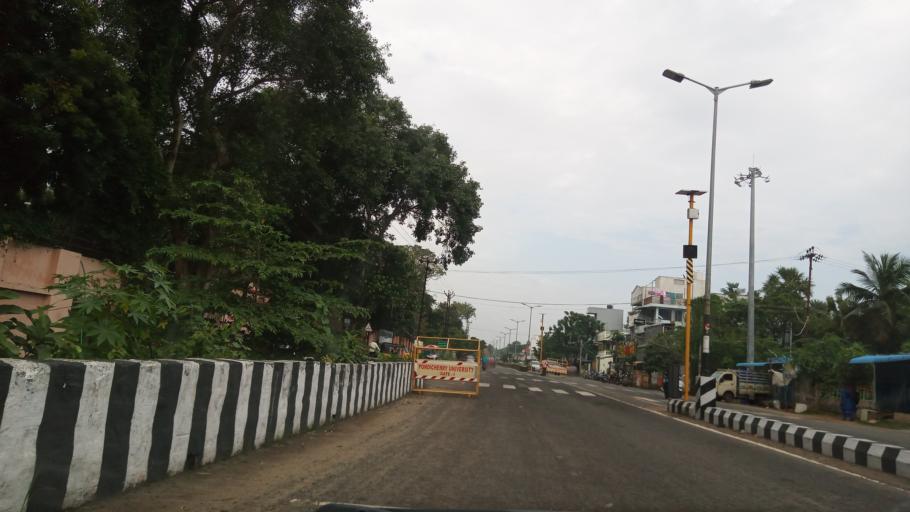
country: IN
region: Tamil Nadu
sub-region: Villupuram
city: Auroville
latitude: 12.0191
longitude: 79.8596
